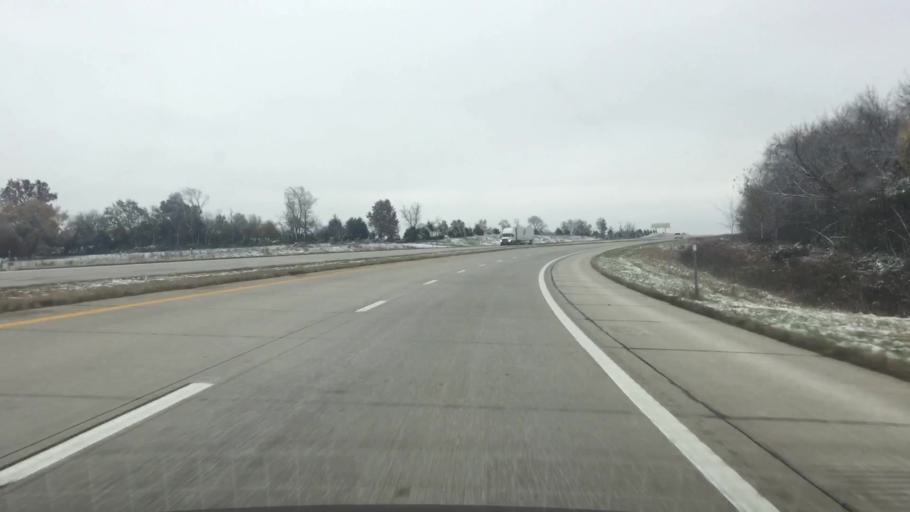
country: US
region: Missouri
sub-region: Saint Clair County
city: Osceola
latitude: 38.1751
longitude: -93.7222
